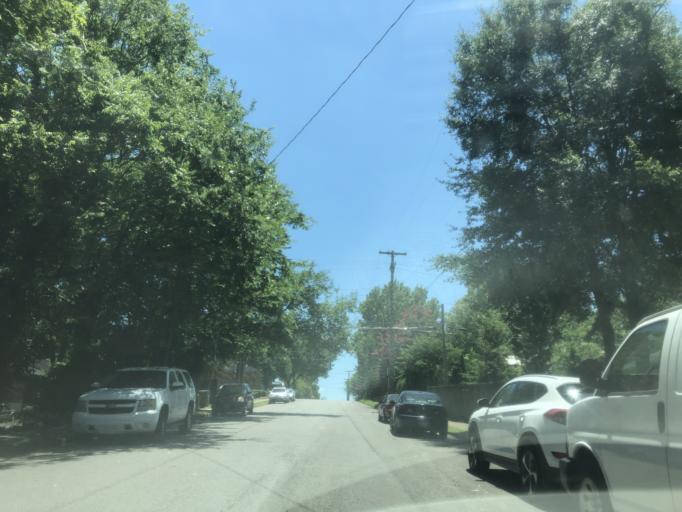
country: US
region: Tennessee
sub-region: Davidson County
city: Nashville
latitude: 36.1727
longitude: -86.7553
